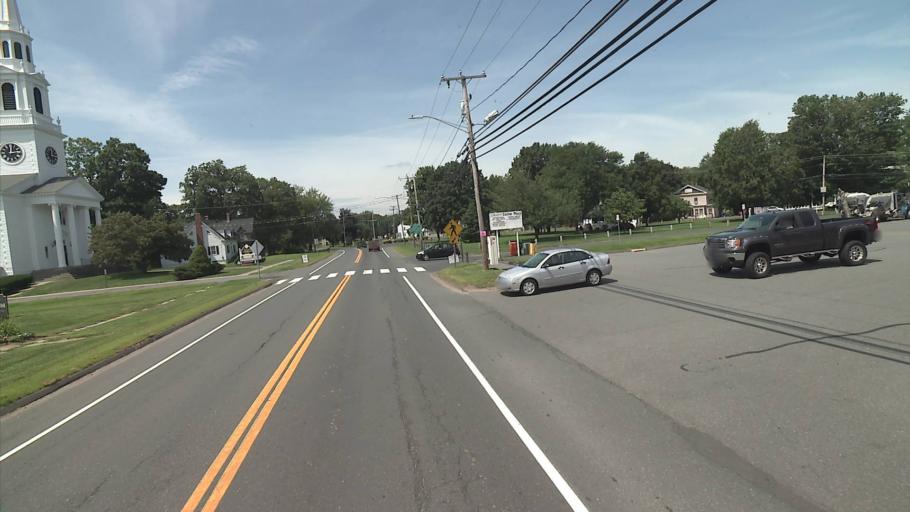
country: US
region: Connecticut
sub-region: Tolland County
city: Ellington
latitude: 41.9037
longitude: -72.4688
